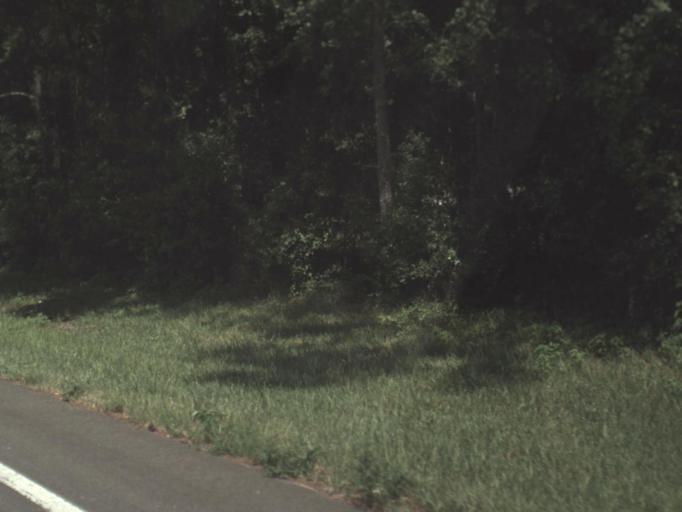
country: US
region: Florida
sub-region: Gilchrist County
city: Trenton
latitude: 29.6353
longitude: -82.7987
